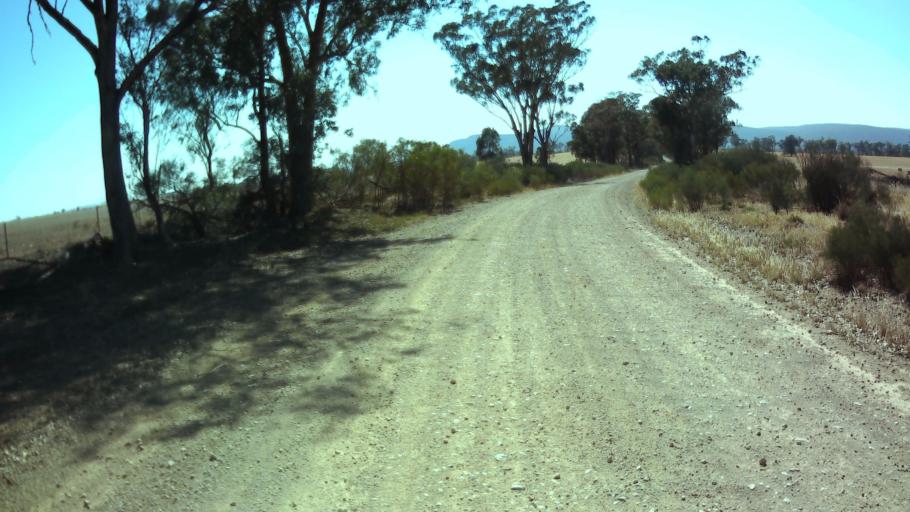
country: AU
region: New South Wales
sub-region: Weddin
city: Grenfell
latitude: -33.9017
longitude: 147.8671
